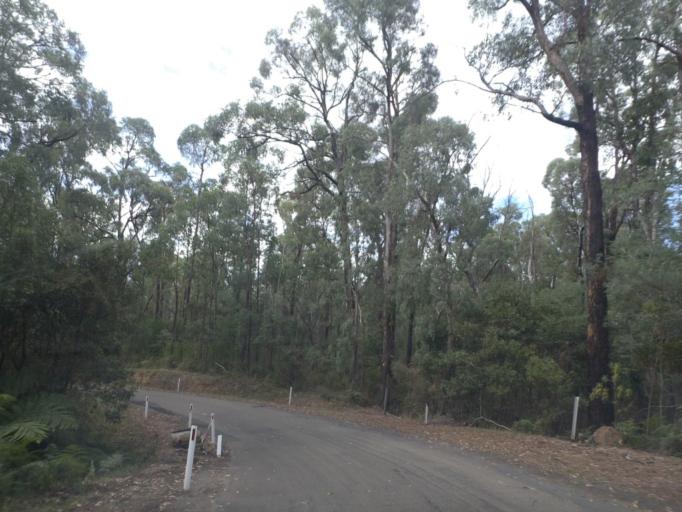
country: AU
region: Victoria
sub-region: Yarra Ranges
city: Healesville
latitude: -37.5453
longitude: 145.6735
